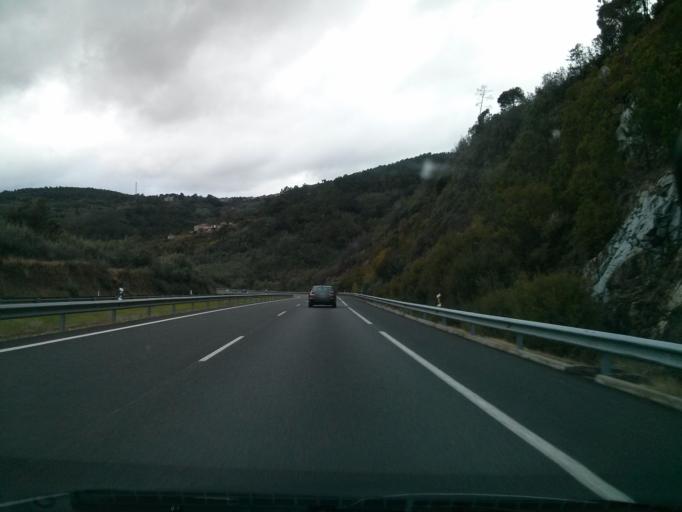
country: ES
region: Galicia
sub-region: Provincia de Ourense
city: Cenlle
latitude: 42.3344
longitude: -8.0630
